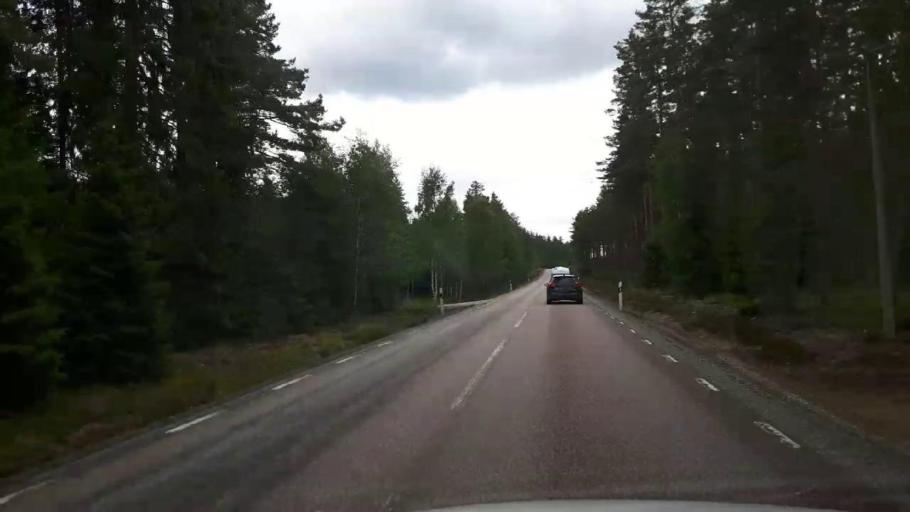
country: SE
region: Vaestmanland
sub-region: Skinnskattebergs Kommun
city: Skinnskatteberg
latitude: 59.8121
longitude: 15.8402
